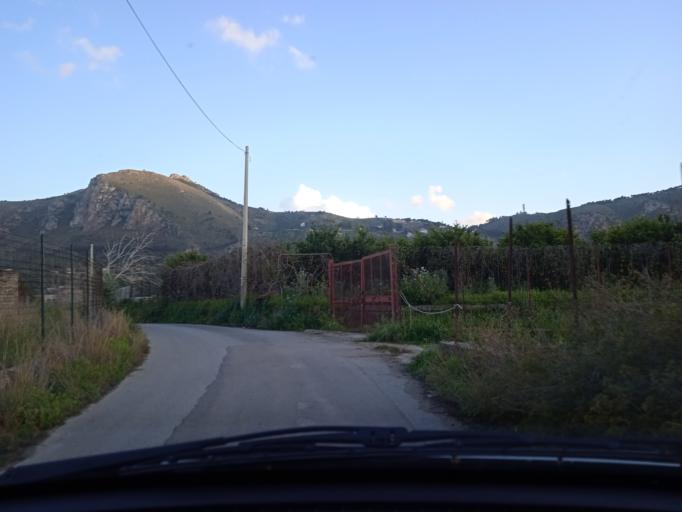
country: IT
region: Sicily
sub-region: Palermo
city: Villabate
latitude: 38.0783
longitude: 13.4267
